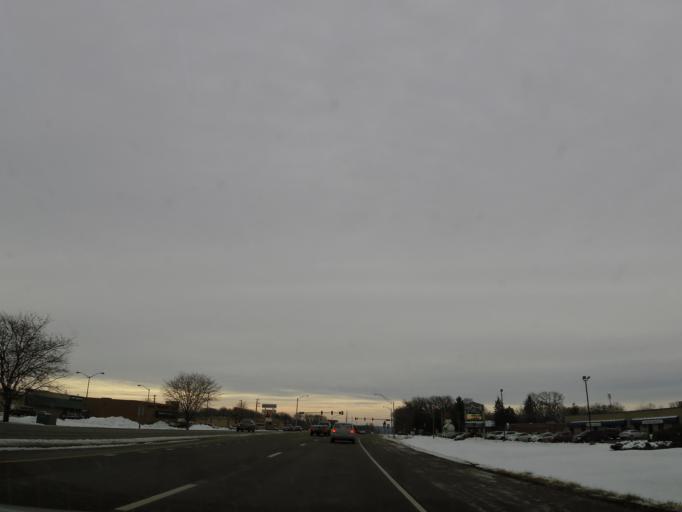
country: US
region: Illinois
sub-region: LaSalle County
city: Peru
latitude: 41.3404
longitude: -89.1203
